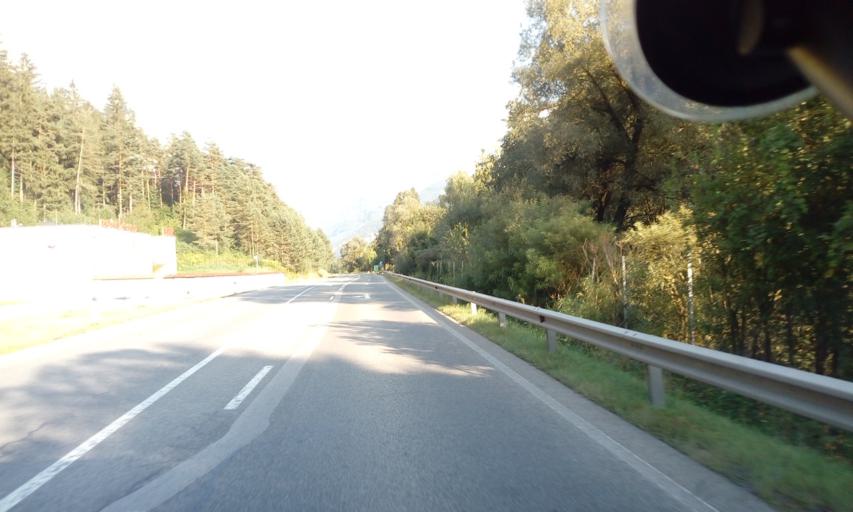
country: AT
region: Carinthia
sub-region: Politischer Bezirk Spittal an der Drau
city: Oberdrauburg
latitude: 46.7560
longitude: 12.9481
